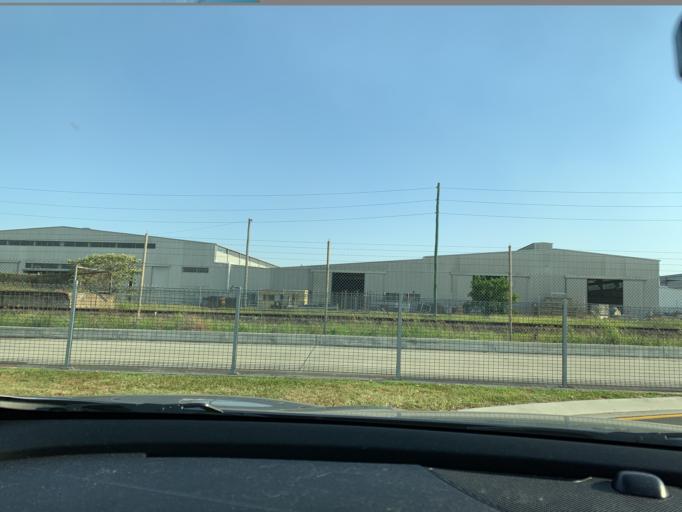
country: AU
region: Queensland
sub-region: Brisbane
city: Ascot
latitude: -27.4290
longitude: 153.0866
